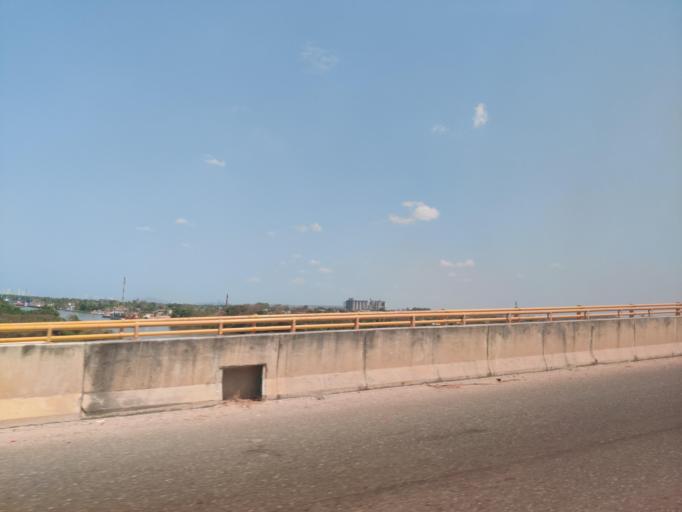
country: CO
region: Bolivar
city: Turbana
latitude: 10.2762
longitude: -75.5199
